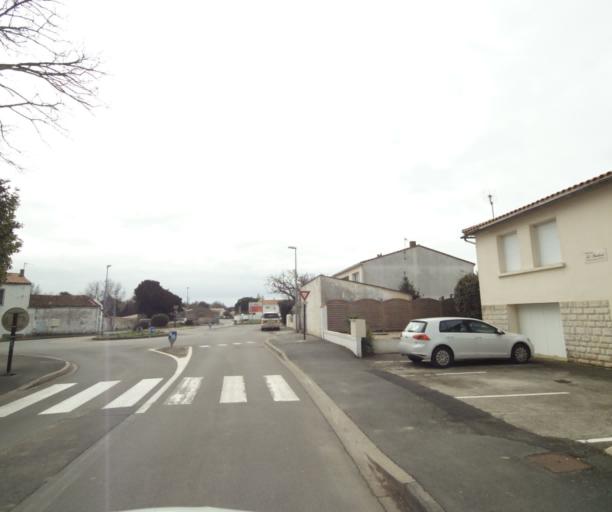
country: FR
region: Poitou-Charentes
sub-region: Departement de la Charente-Maritime
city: Lagord
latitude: 46.1864
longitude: -1.1664
